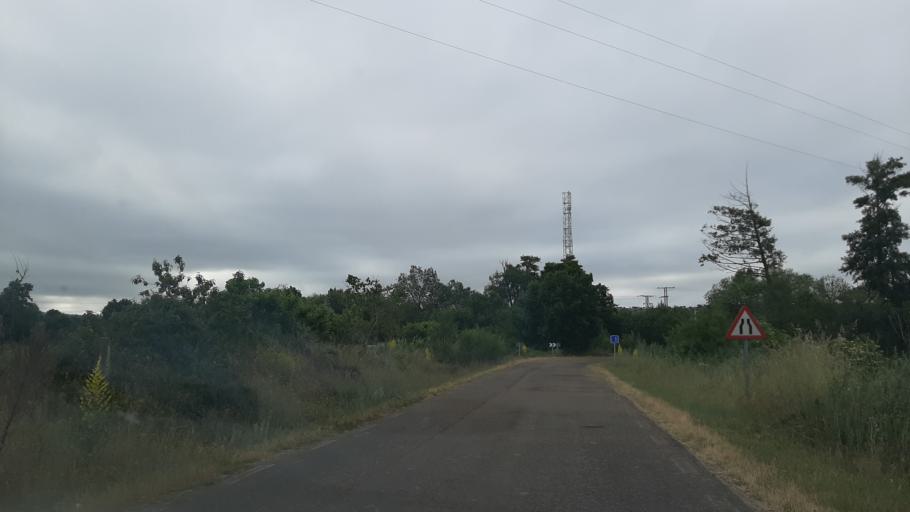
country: ES
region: Castille and Leon
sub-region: Provincia de Salamanca
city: Pastores
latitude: 40.5648
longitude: -6.4858
